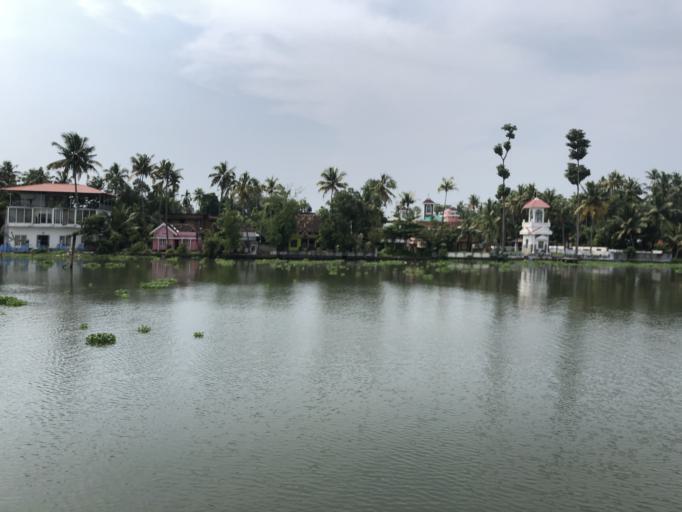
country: IN
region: Kerala
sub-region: Ernakulam
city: Cochin
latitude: 9.9952
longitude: 76.2663
